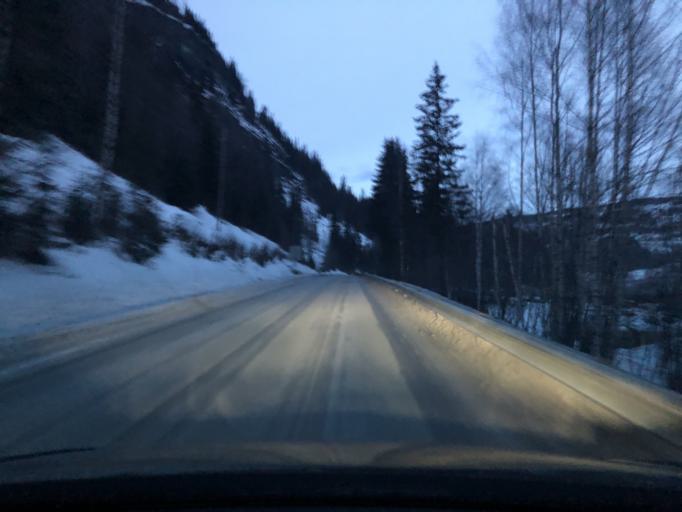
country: NO
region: Oppland
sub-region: Nord-Aurdal
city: Fagernes
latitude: 60.9999
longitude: 9.2100
